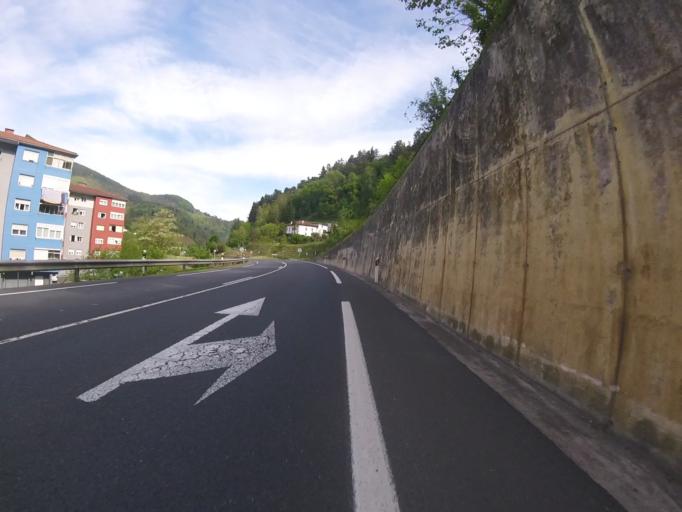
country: ES
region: Basque Country
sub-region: Provincia de Guipuzcoa
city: Urretxu
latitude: 43.0946
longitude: -2.3118
